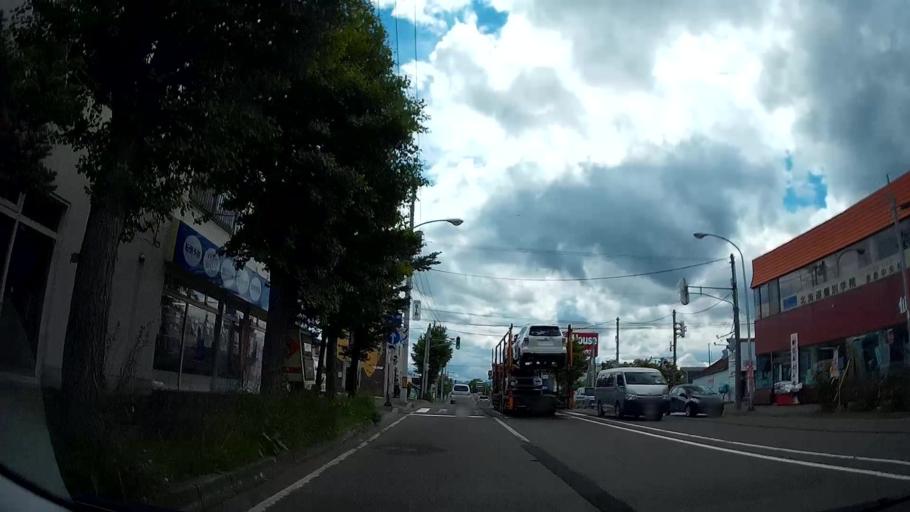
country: JP
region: Hokkaido
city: Kitahiroshima
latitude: 42.8814
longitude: 141.5734
